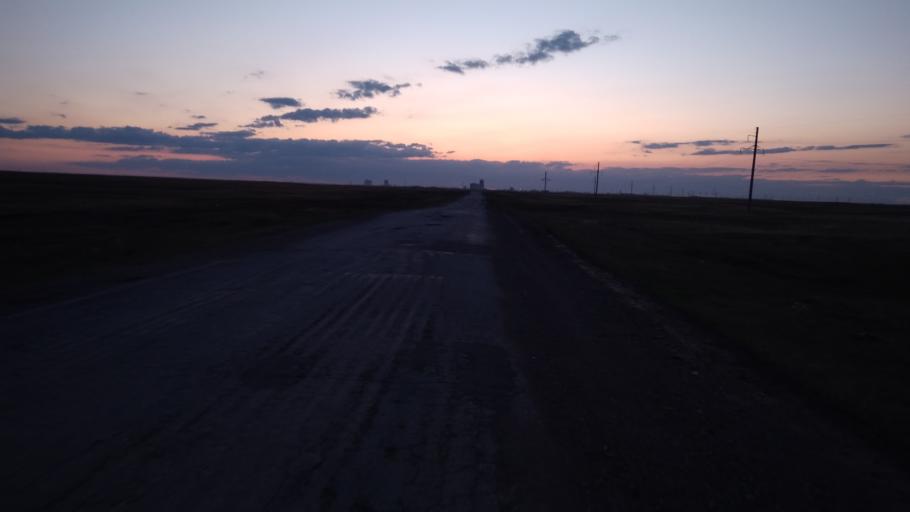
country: RU
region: Chelyabinsk
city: Troitsk
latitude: 54.0911
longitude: 61.6444
